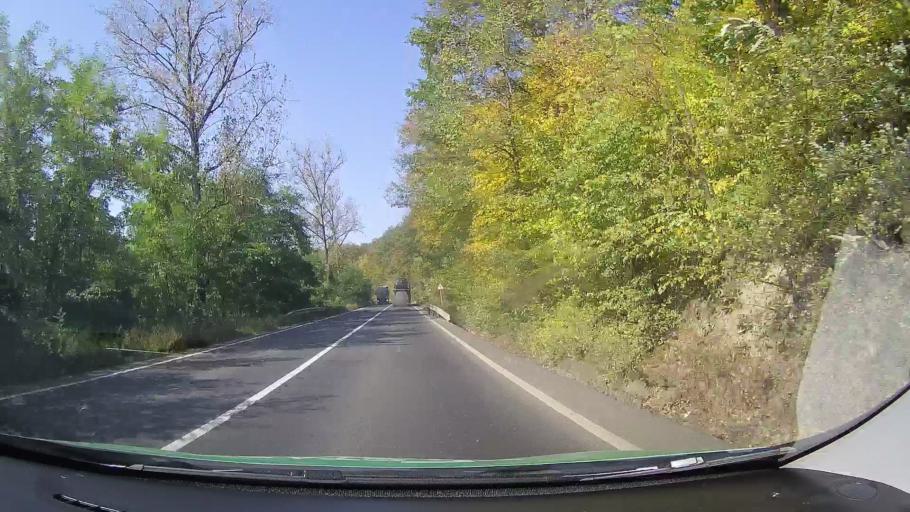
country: RO
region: Arad
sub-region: Comuna Varadia de Mures
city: Varadia de Mures
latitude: 46.0296
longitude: 22.1193
